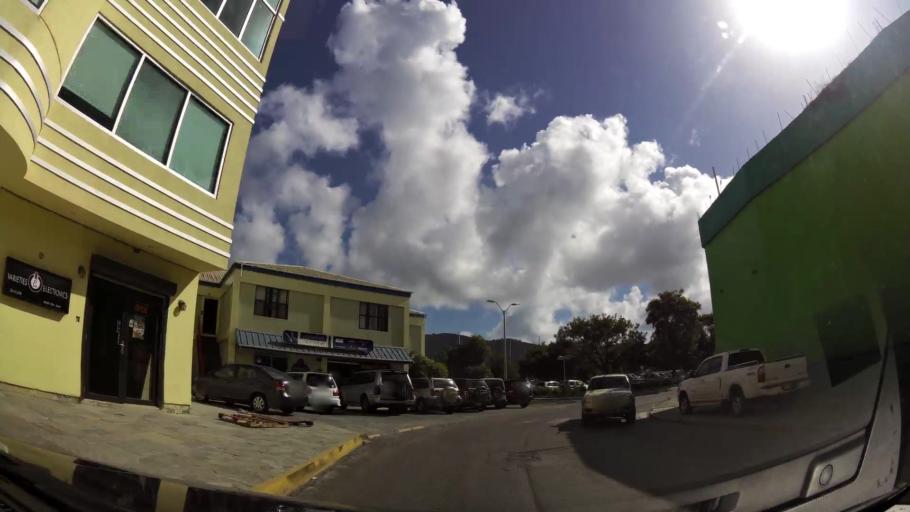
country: VG
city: Road Town
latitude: 18.4237
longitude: -64.6200
